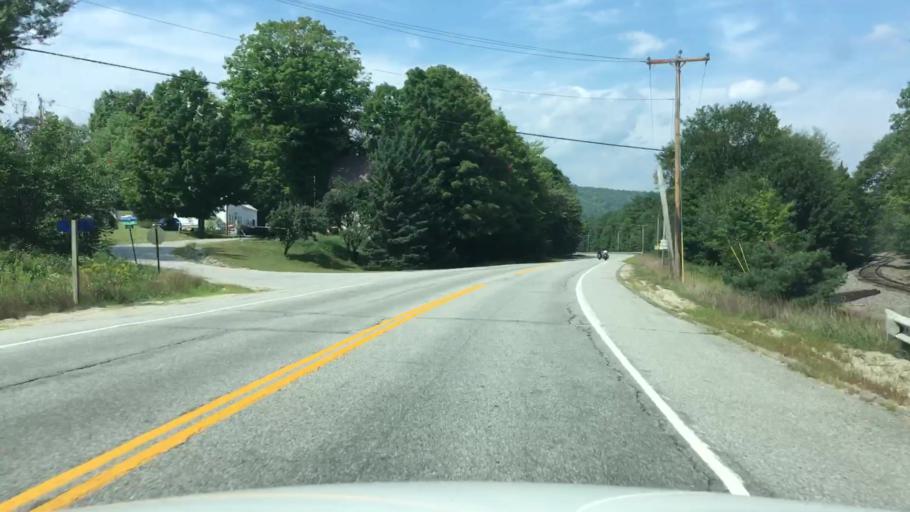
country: US
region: Maine
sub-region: Oxford County
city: Peru
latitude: 44.5064
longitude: -70.4050
